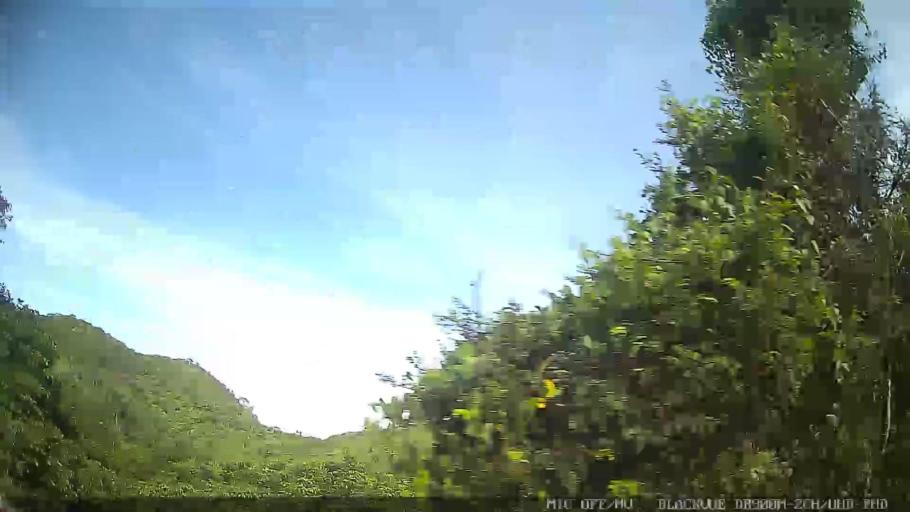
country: BR
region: Sao Paulo
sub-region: Amparo
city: Amparo
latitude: -22.6970
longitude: -46.6904
